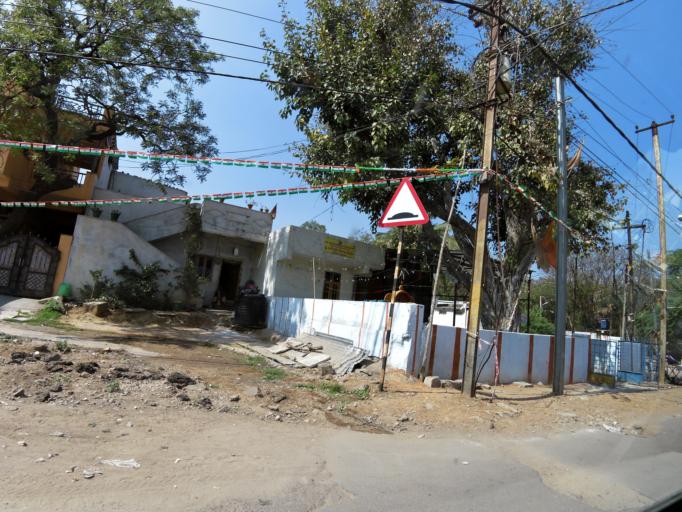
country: IN
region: Telangana
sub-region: Hyderabad
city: Hyderabad
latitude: 17.3928
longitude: 78.4000
